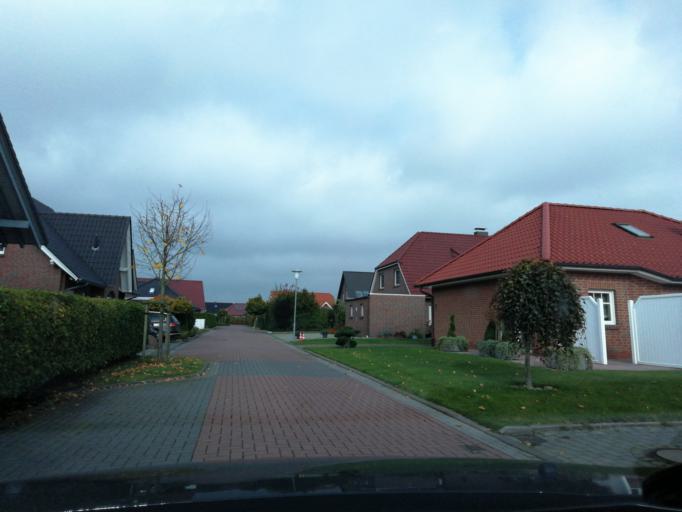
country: DE
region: Lower Saxony
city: Fedderwarden
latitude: 53.6313
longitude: 8.0312
